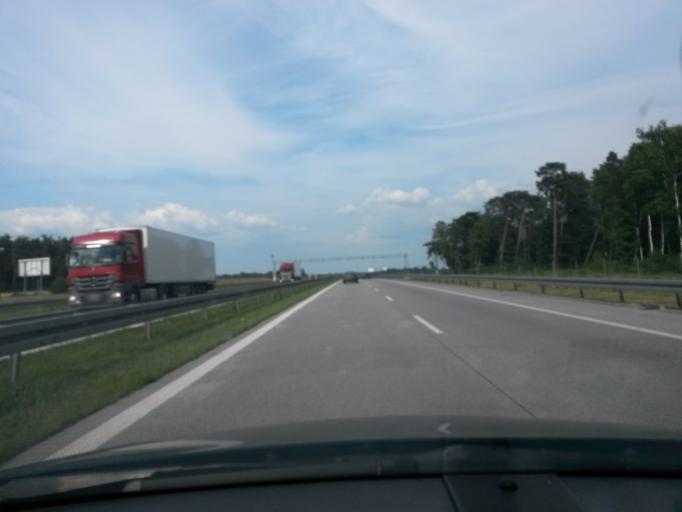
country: PL
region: Lodz Voivodeship
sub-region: Powiat tomaszowski
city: Czerniewice
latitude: 51.6851
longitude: 20.1997
